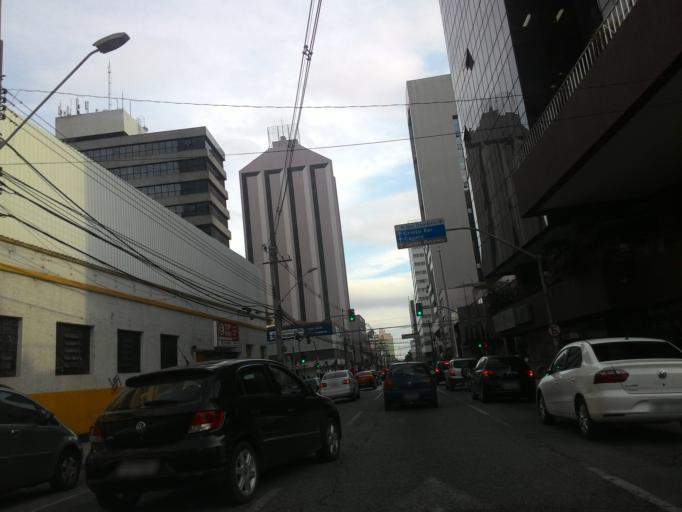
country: BR
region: Parana
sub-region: Curitiba
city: Curitiba
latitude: -25.4286
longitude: -49.2643
